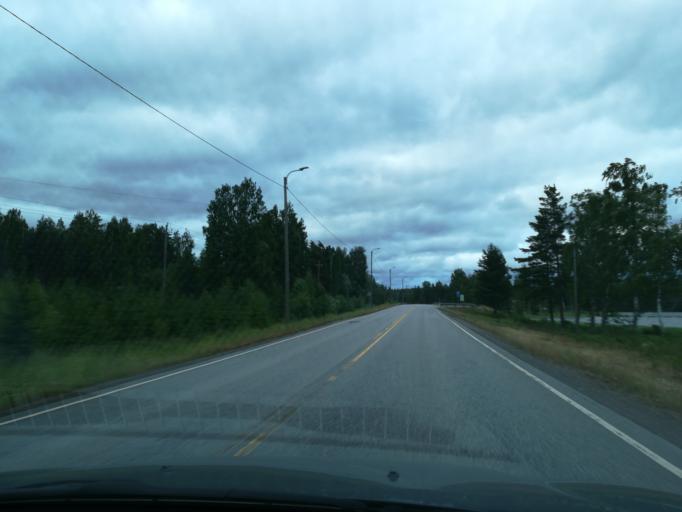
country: FI
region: Southern Savonia
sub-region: Mikkeli
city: Ristiina
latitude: 61.3518
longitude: 27.3966
